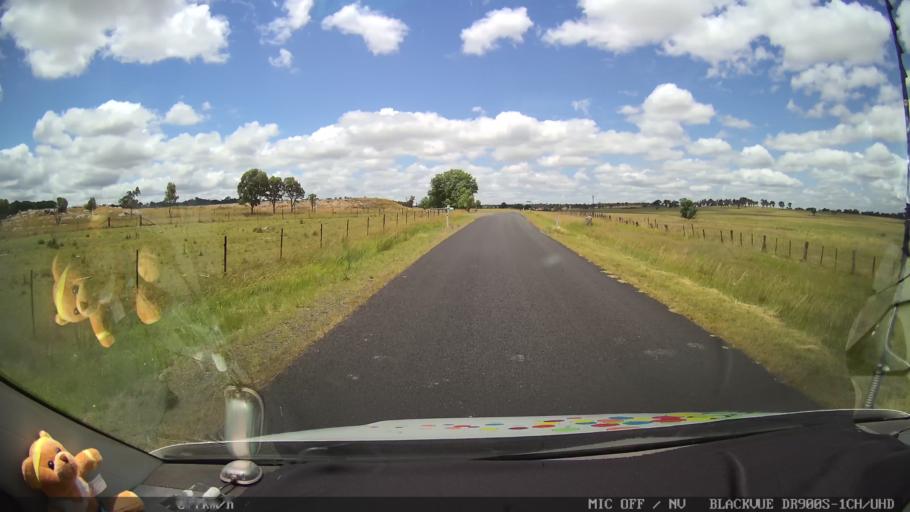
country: AU
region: New South Wales
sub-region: Glen Innes Severn
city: Glen Innes
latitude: -29.4219
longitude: 151.7372
